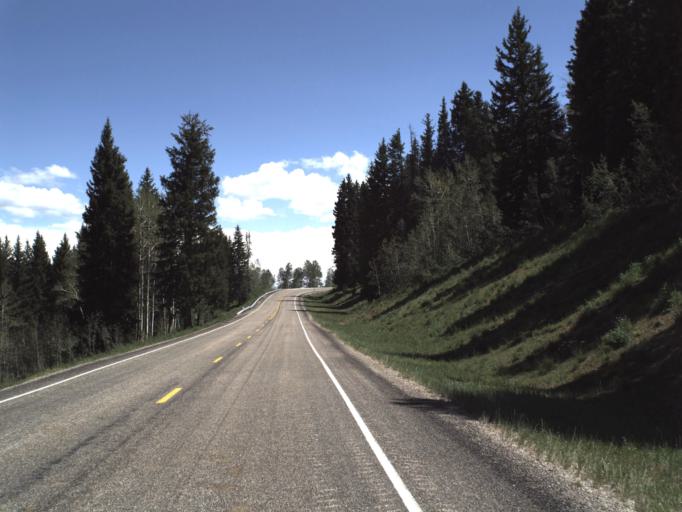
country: US
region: Utah
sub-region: Weber County
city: Wolf Creek
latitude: 41.4595
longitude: -111.5029
